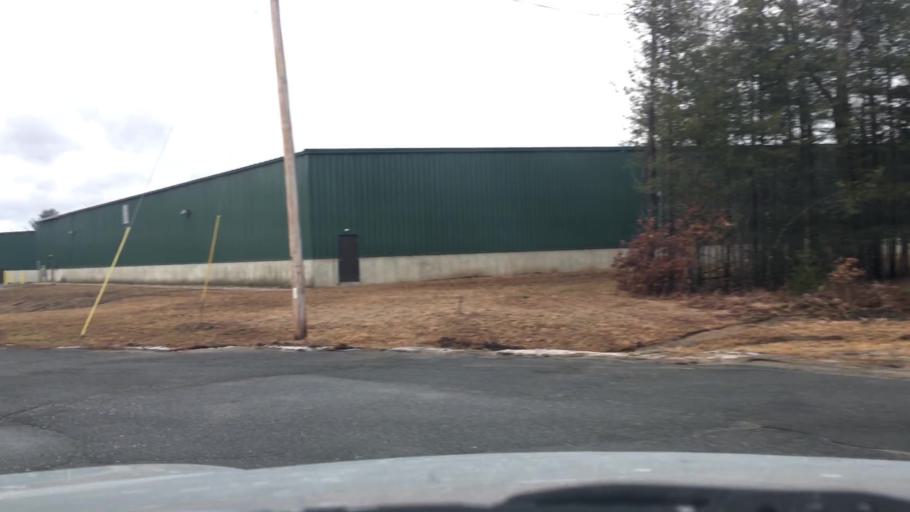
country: US
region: Massachusetts
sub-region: Franklin County
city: Orange
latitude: 42.5659
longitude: -72.2827
